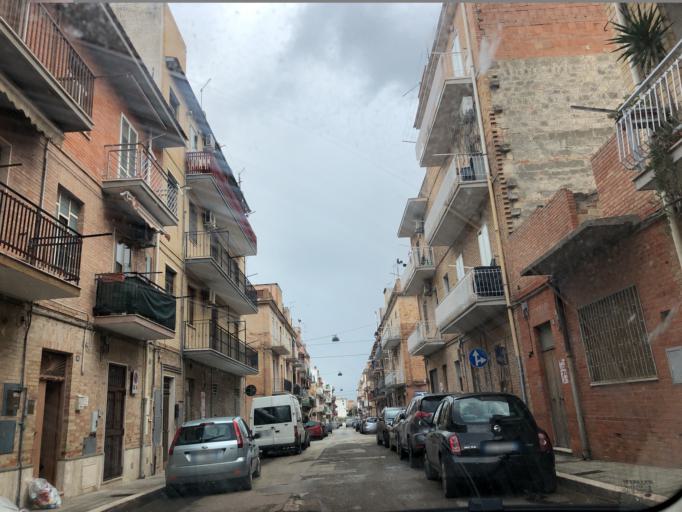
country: IT
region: Apulia
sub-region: Provincia di Foggia
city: Lucera
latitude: 41.5037
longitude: 15.3394
